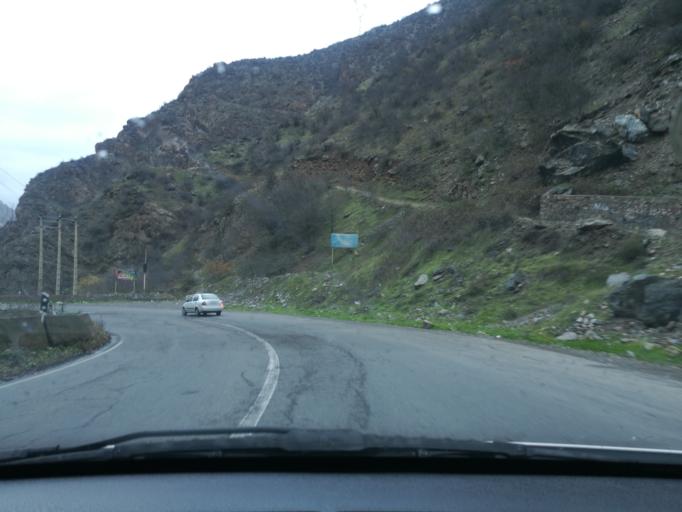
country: IR
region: Mazandaran
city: Chalus
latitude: 36.3043
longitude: 51.2480
